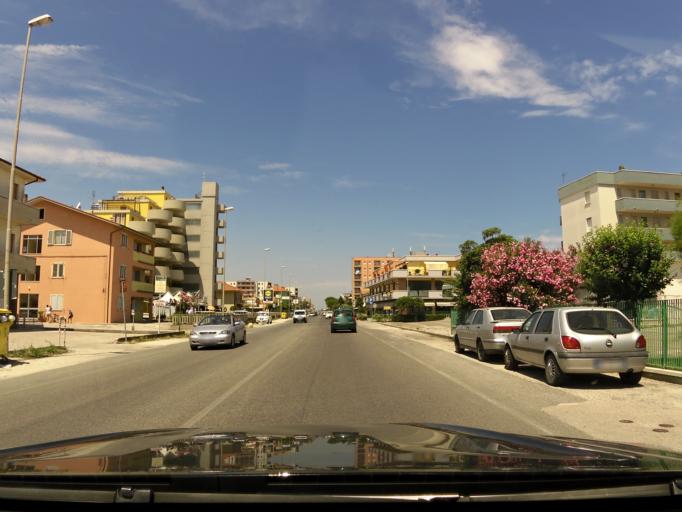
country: IT
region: The Marches
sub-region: Provincia di Pesaro e Urbino
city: Marotta
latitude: 43.7596
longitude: 13.1531
